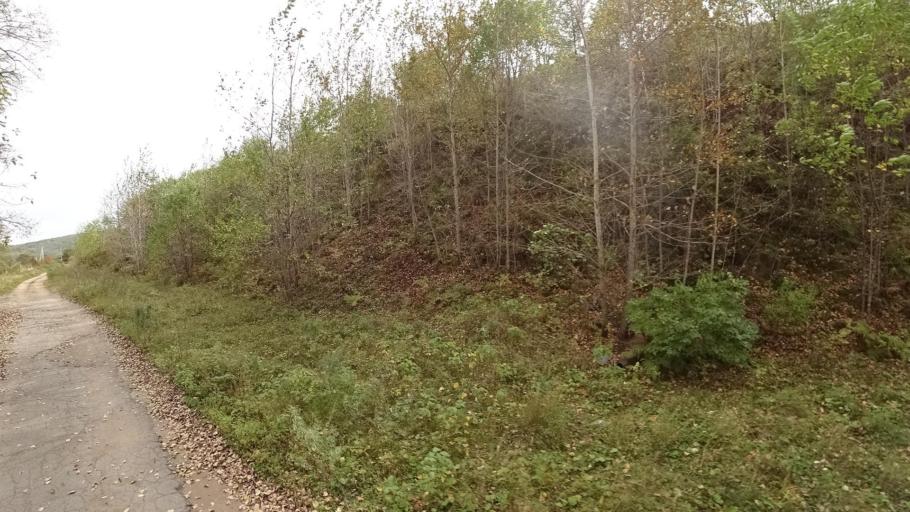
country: RU
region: Jewish Autonomous Oblast
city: Khingansk
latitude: 49.1240
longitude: 131.1985
